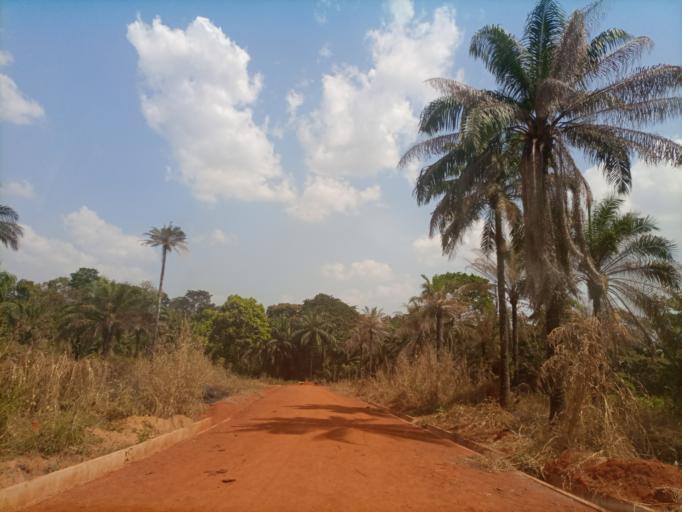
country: NG
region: Enugu
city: Obolo-Eke (1)
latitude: 6.8641
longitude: 7.6602
